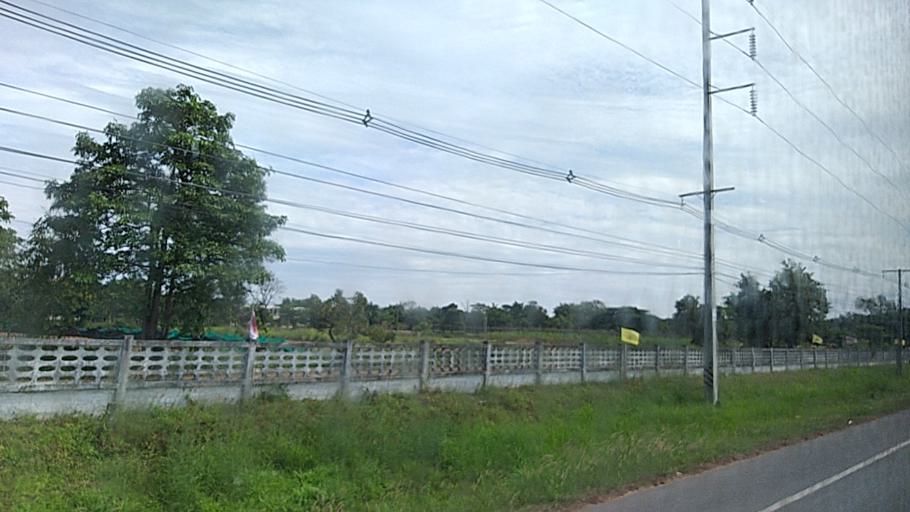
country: TH
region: Maha Sarakham
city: Chiang Yuen
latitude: 16.4414
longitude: 103.0440
